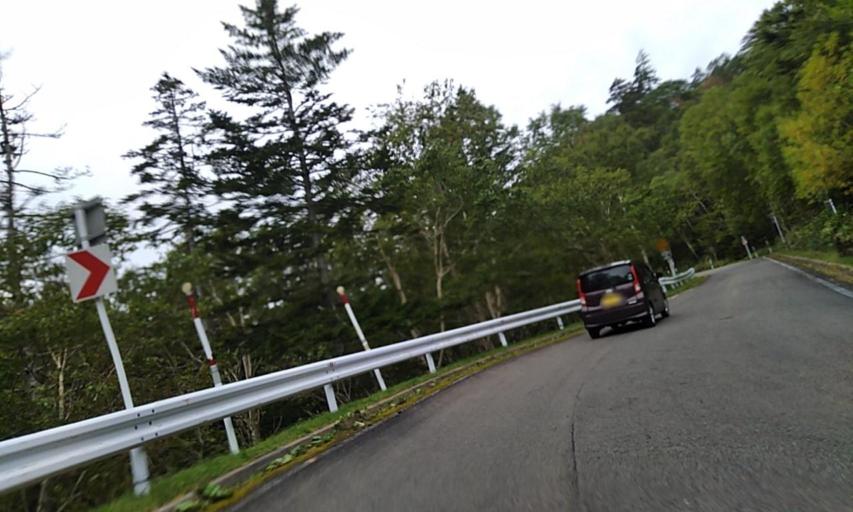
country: JP
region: Hokkaido
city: Bihoro
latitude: 43.5685
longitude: 144.2311
